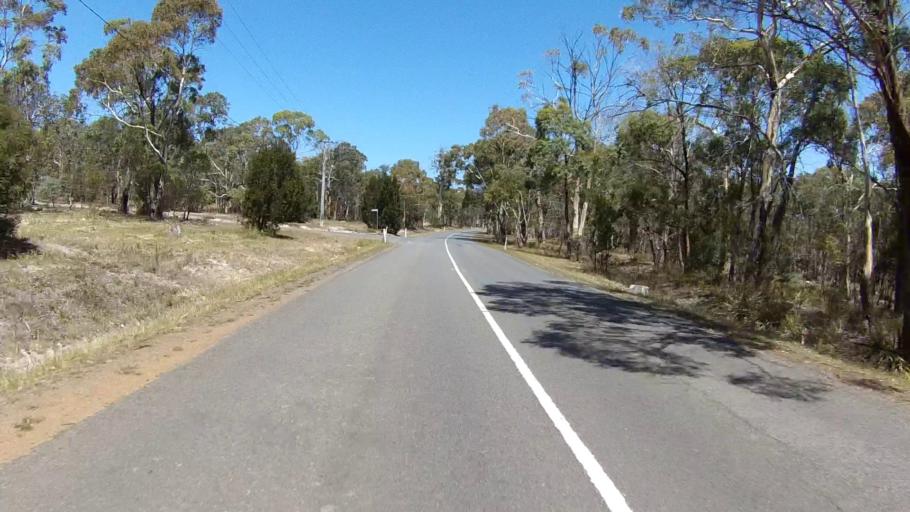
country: AU
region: Tasmania
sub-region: Clarence
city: Sandford
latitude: -42.9702
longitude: 147.4798
